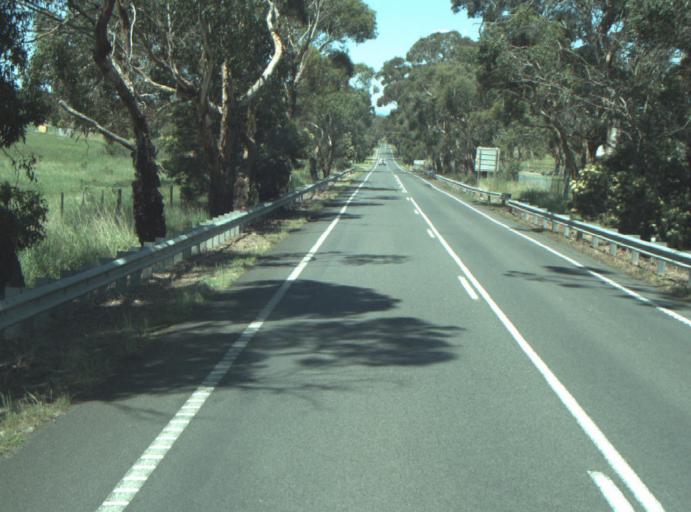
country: AU
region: Victoria
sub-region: Greater Geelong
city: Lara
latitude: -37.8876
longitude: 144.2572
